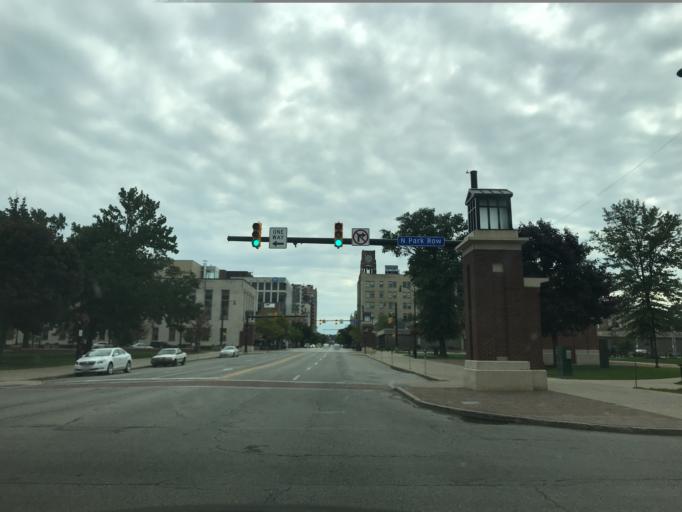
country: US
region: Pennsylvania
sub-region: Erie County
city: Erie
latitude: 42.1299
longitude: -80.0856
